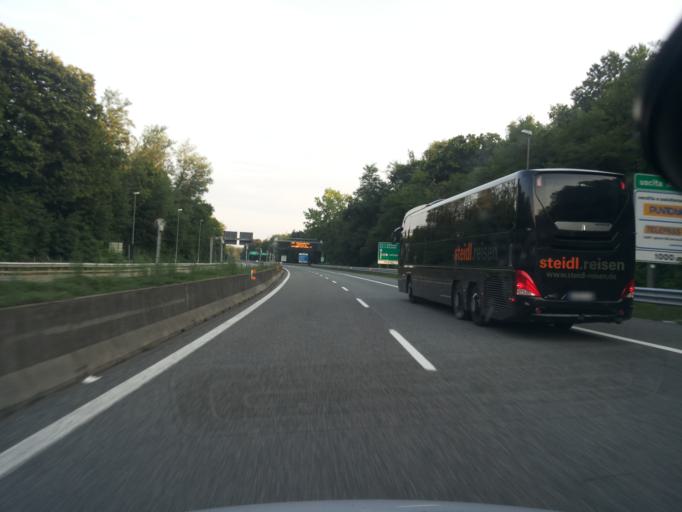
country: IT
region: Piedmont
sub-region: Provincia di Novara
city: Paruzzaro
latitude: 45.7389
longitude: 8.5039
